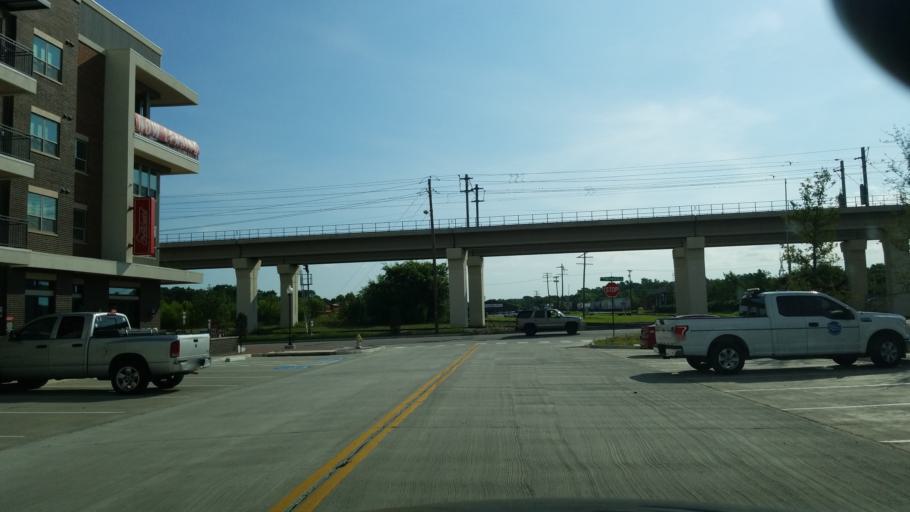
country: US
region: Texas
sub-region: Dallas County
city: Carrollton
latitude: 32.9548
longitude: -96.9095
